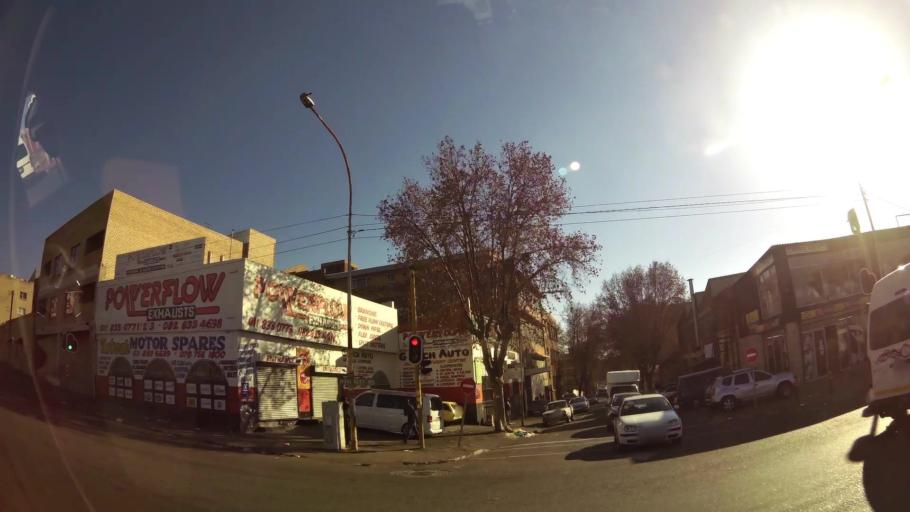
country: ZA
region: Gauteng
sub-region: City of Johannesburg Metropolitan Municipality
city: Johannesburg
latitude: -26.2090
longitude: 28.0240
